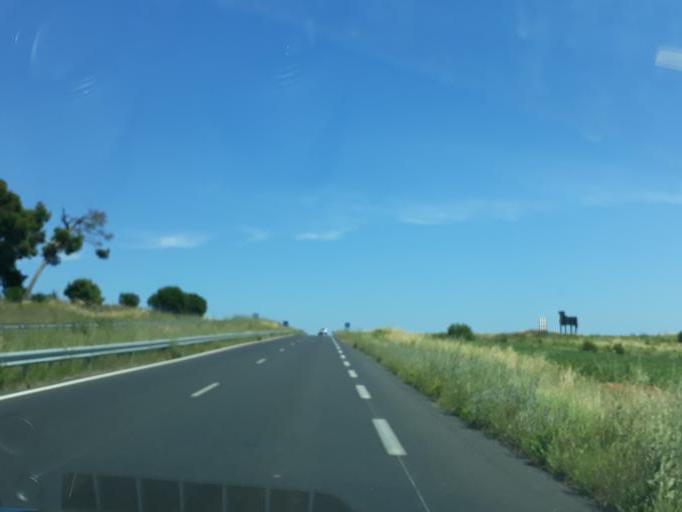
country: FR
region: Languedoc-Roussillon
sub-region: Departement de l'Herault
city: Portiragnes
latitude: 43.3140
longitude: 3.3199
